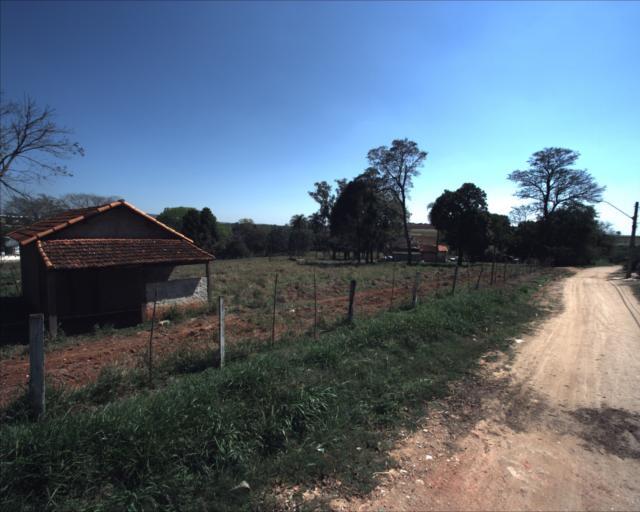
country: BR
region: Sao Paulo
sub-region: Aracoiaba Da Serra
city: Aracoiaba da Serra
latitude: -23.4405
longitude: -47.5395
